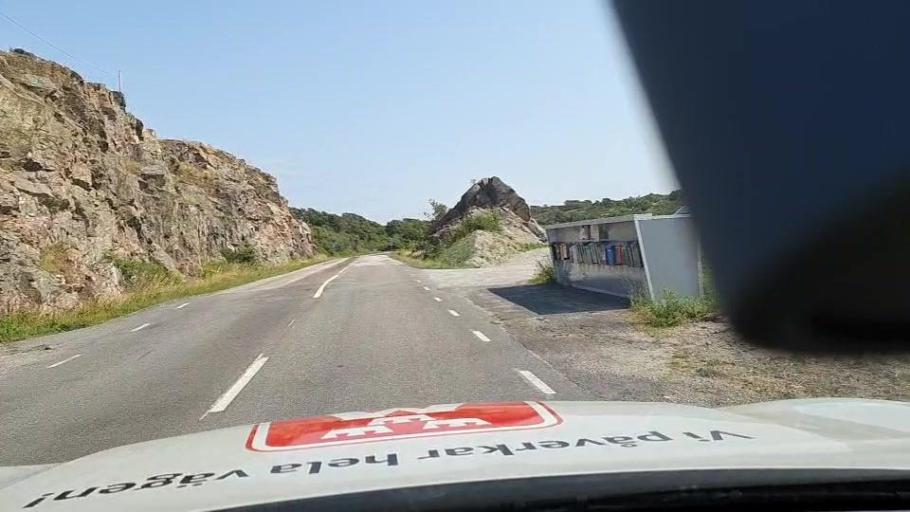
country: SE
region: Vaestra Goetaland
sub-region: Tjorns Kommun
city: Skaerhamn
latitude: 58.0976
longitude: 11.4891
